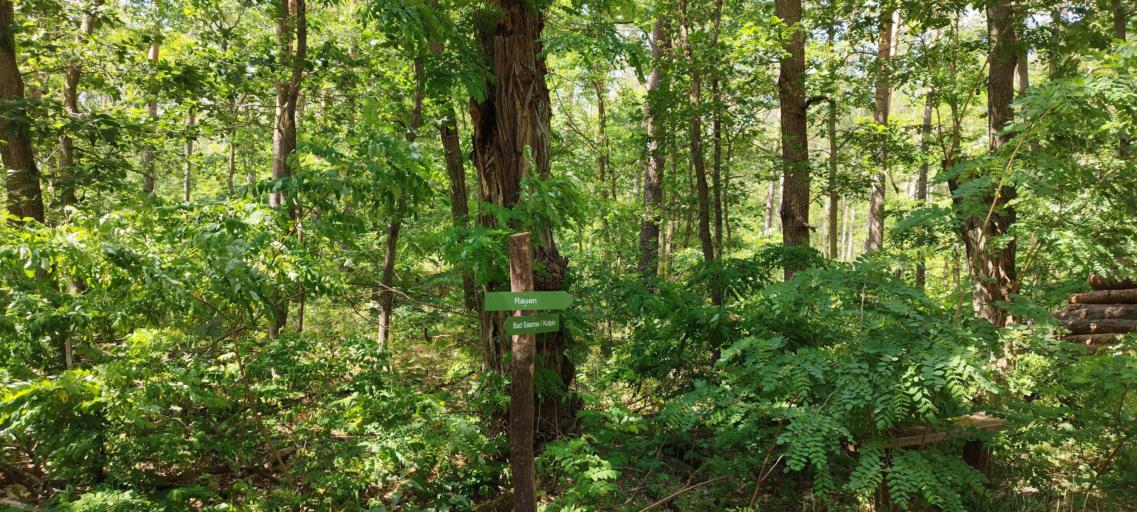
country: DE
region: Brandenburg
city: Rauen
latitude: 52.3117
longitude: 14.0278
